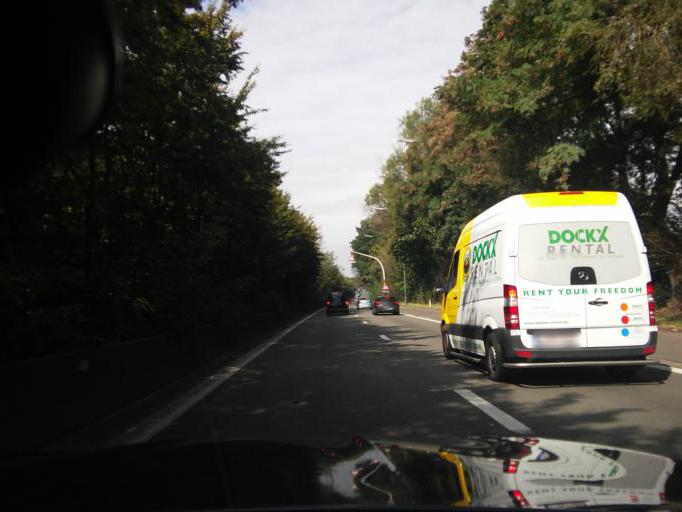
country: BE
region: Flanders
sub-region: Provincie Vlaams-Brabant
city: Halle
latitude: 50.7211
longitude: 4.2409
